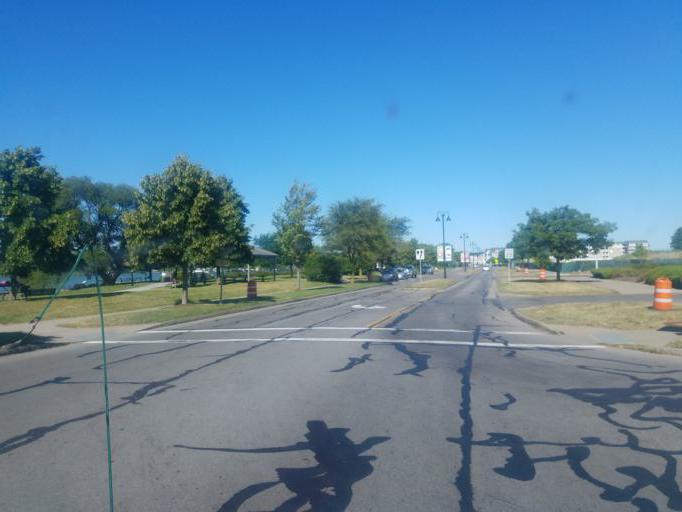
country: US
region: New York
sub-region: Ontario County
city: Canandaigua
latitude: 42.8750
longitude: -77.2634
